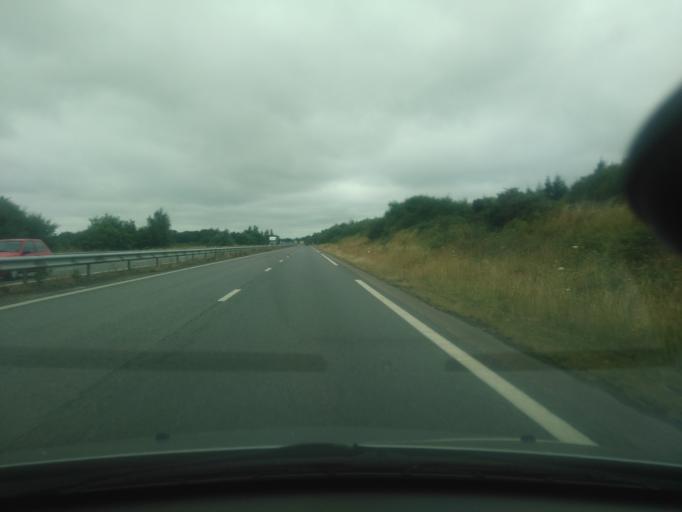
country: FR
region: Brittany
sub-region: Departement des Cotes-d'Armor
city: Plelan-le-Petit
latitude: 48.4203
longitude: -2.2679
